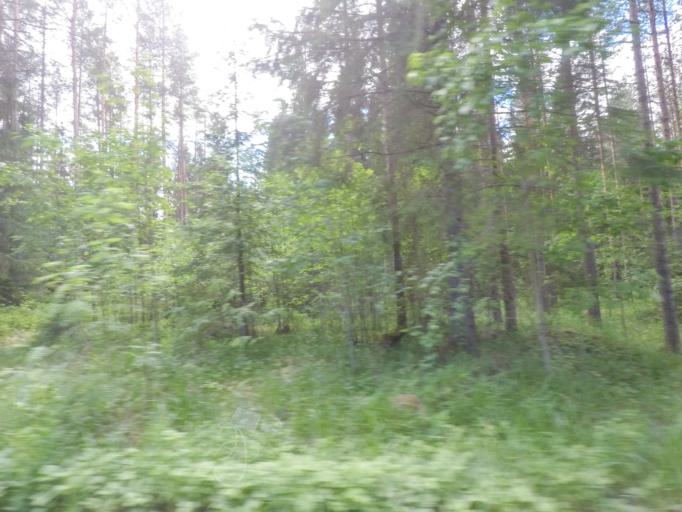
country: FI
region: Central Finland
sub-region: Jyvaeskylae
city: Hankasalmi
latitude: 62.4104
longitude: 26.6472
